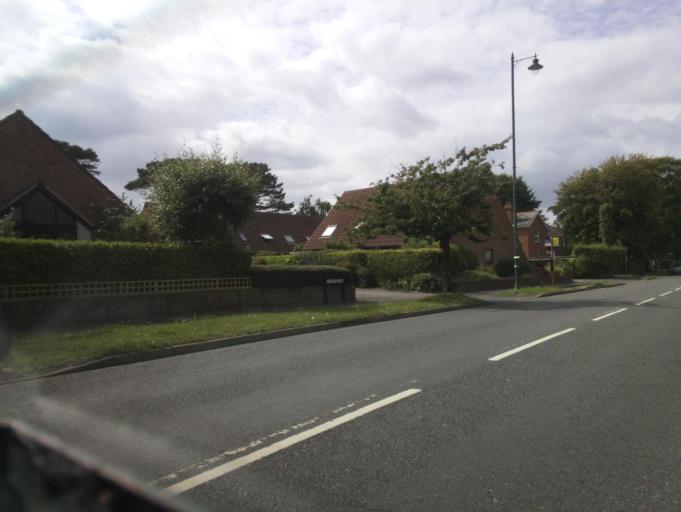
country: GB
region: England
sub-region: Hampshire
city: New Milton
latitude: 50.7485
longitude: -1.6521
